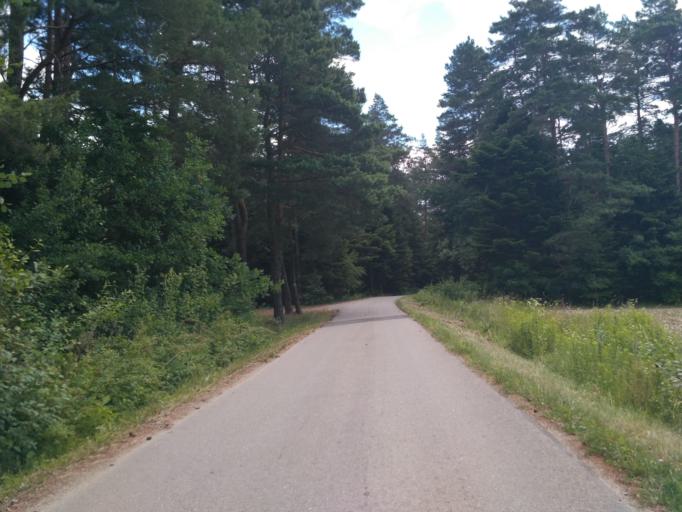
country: PL
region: Subcarpathian Voivodeship
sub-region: Powiat jasielski
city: Brzyska
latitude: 49.8073
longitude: 21.3796
